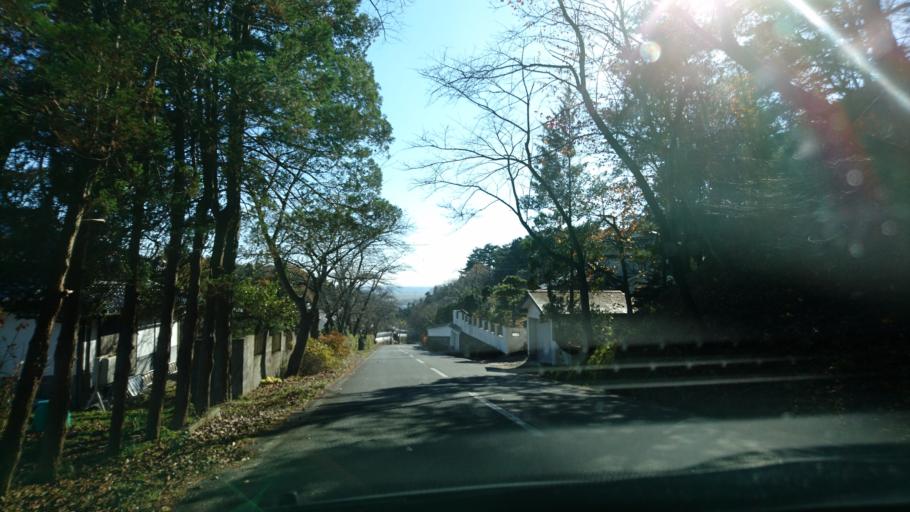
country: JP
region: Iwate
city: Ichinoseki
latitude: 38.9927
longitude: 141.1067
